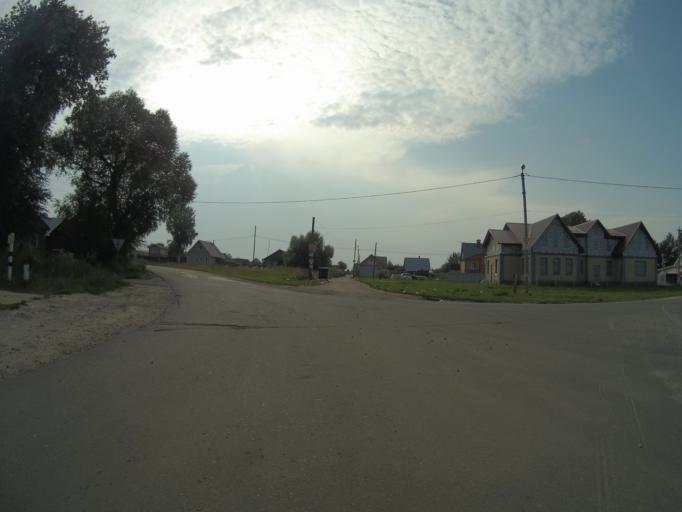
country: RU
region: Vladimir
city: Suzdal'
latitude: 56.4279
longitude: 40.4174
